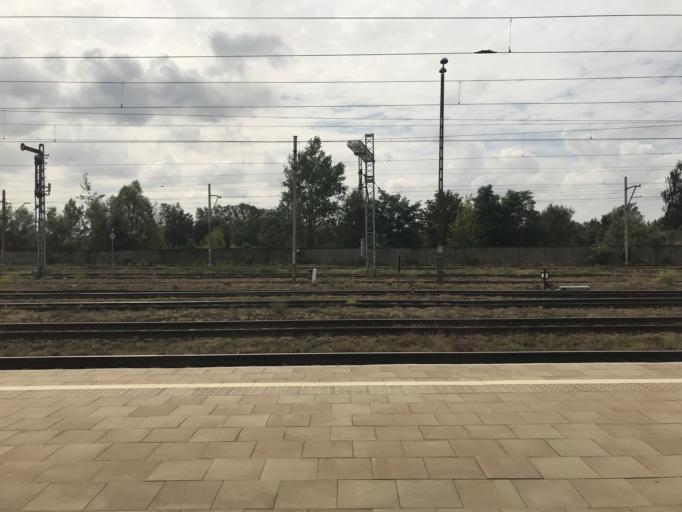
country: PL
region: Greater Poland Voivodeship
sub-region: Powiat gnieznienski
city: Gniezno
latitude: 52.5295
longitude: 17.6044
